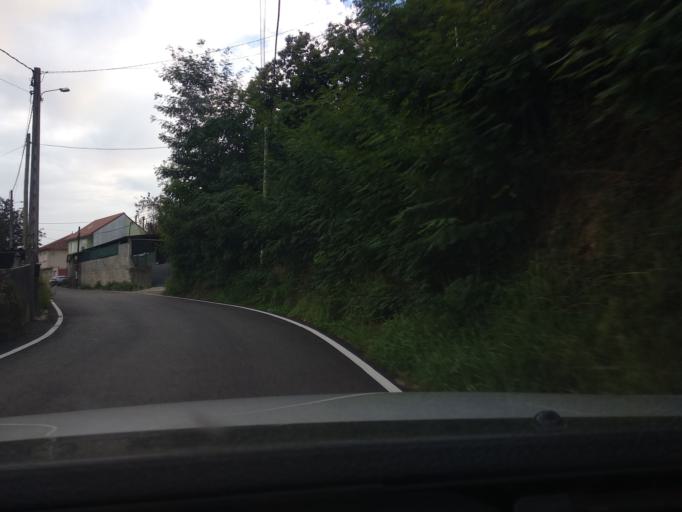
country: ES
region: Galicia
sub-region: Provincia de Pontevedra
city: Moana
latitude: 42.2930
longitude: -8.7388
